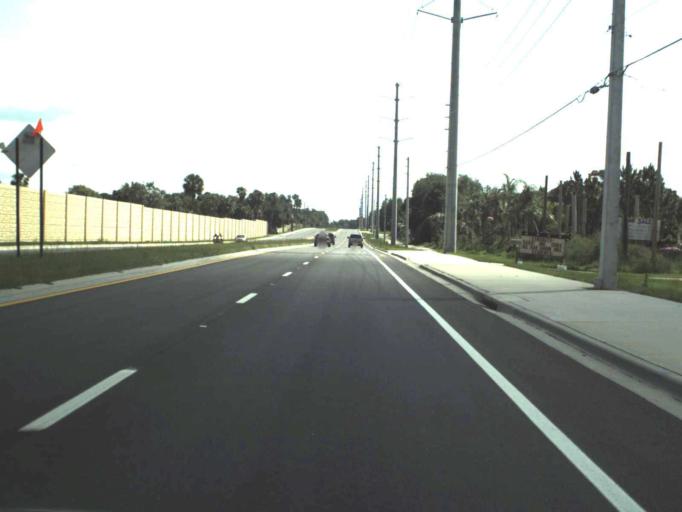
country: US
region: Florida
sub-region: Seminole County
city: Midway
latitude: 28.8360
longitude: -81.1719
